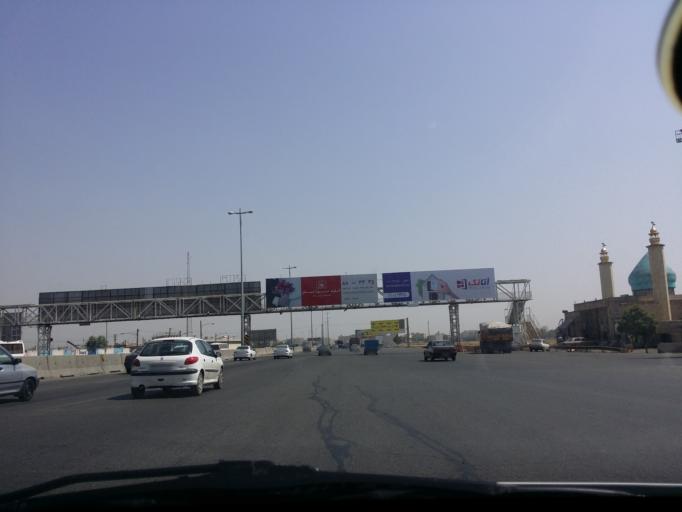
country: IR
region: Alborz
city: Karaj
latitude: 35.8370
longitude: 50.9098
